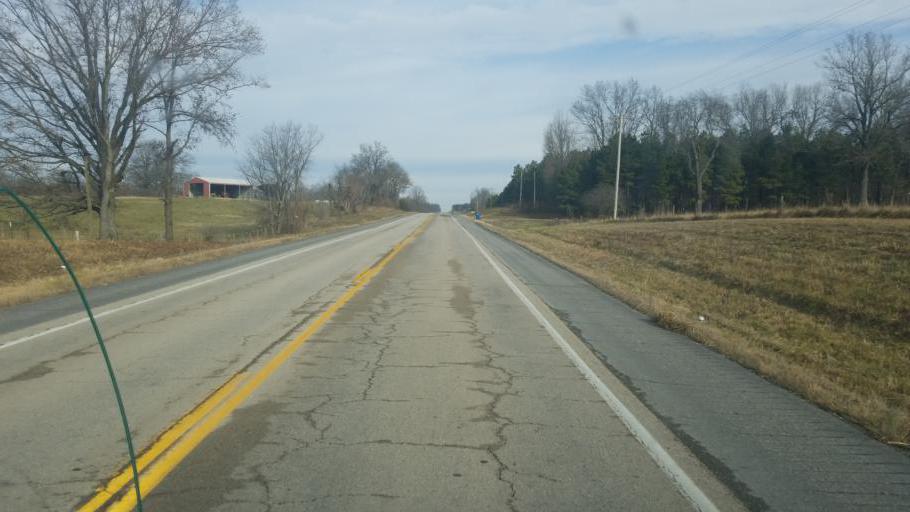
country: US
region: Missouri
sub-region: Stoddard County
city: Bloomfield
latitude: 36.9665
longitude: -89.9061
